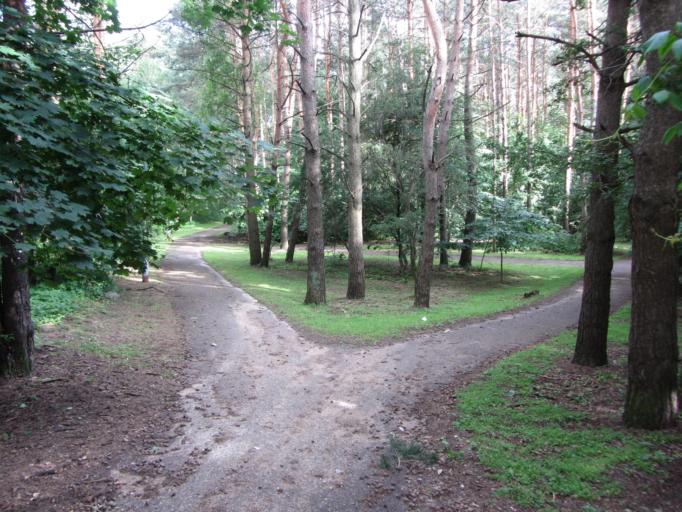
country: LT
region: Vilnius County
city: Lazdynai
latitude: 54.6834
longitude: 25.2044
